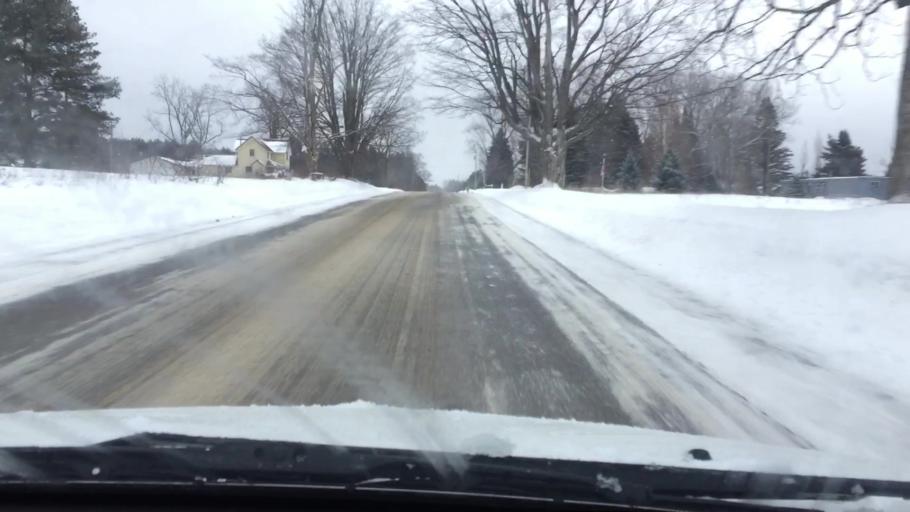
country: US
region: Michigan
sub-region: Kalkaska County
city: Kalkaska
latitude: 44.6405
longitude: -85.1894
